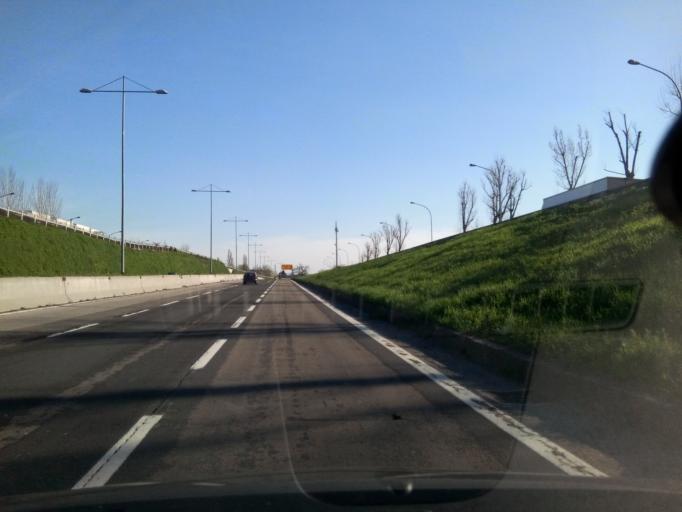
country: IT
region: Emilia-Romagna
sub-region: Provincia di Bologna
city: Casalecchio di Reno
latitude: 44.4949
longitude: 11.2962
